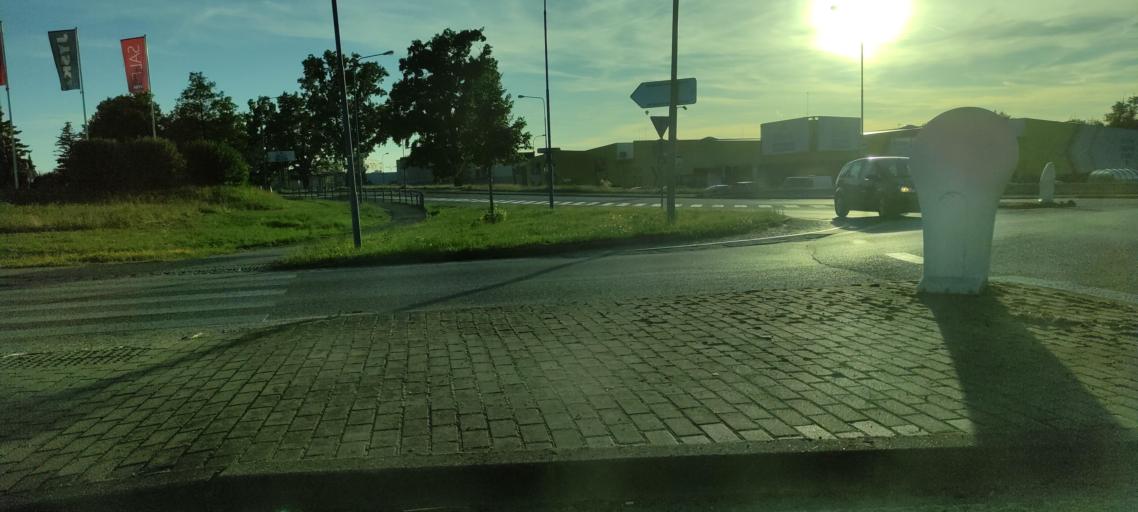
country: CZ
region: Jihocesky
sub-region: Okres Jindrichuv Hradec
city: Jindrichuv Hradec
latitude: 49.1436
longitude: 15.0239
